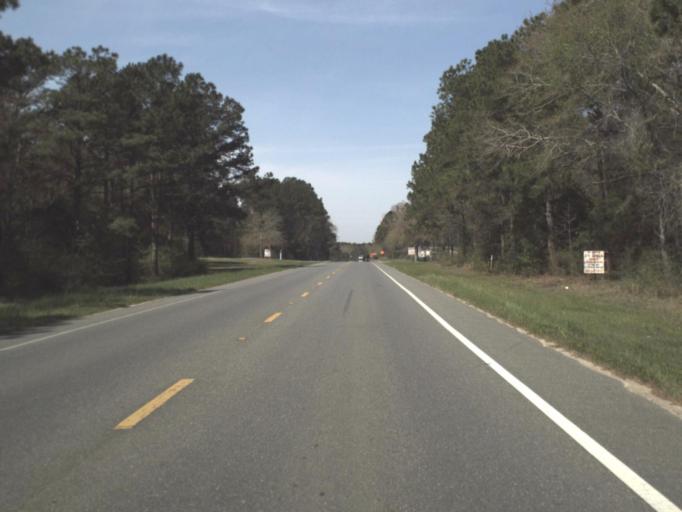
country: US
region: Florida
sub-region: Holmes County
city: Bonifay
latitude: 30.7794
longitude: -85.6321
